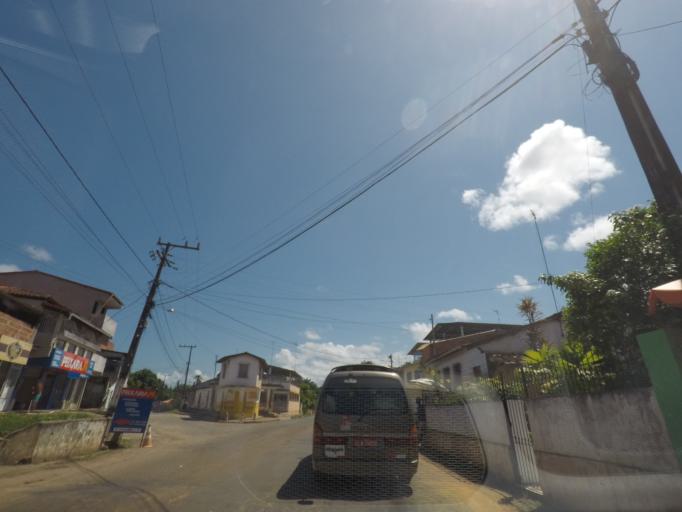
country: BR
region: Bahia
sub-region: Valenca
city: Valenca
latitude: -13.4393
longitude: -39.0801
